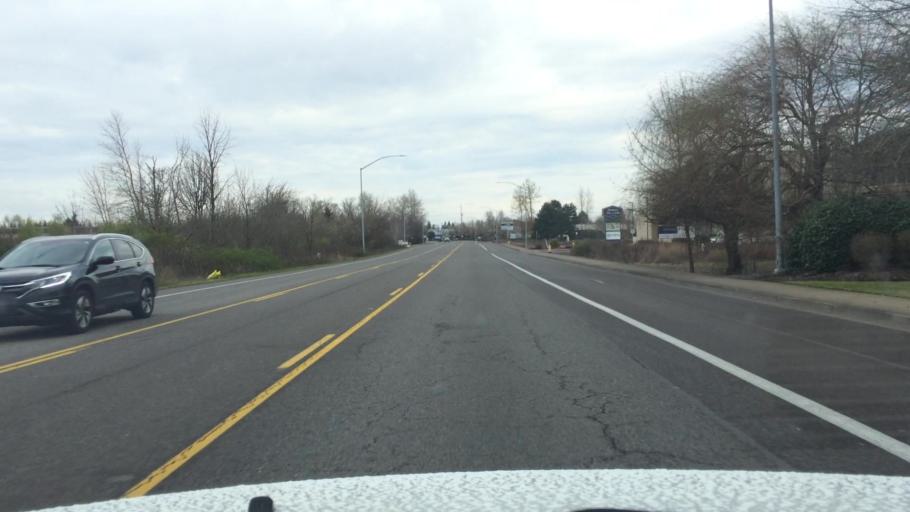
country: US
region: Oregon
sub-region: Marion County
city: Four Corners
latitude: 44.9232
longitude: -122.9947
